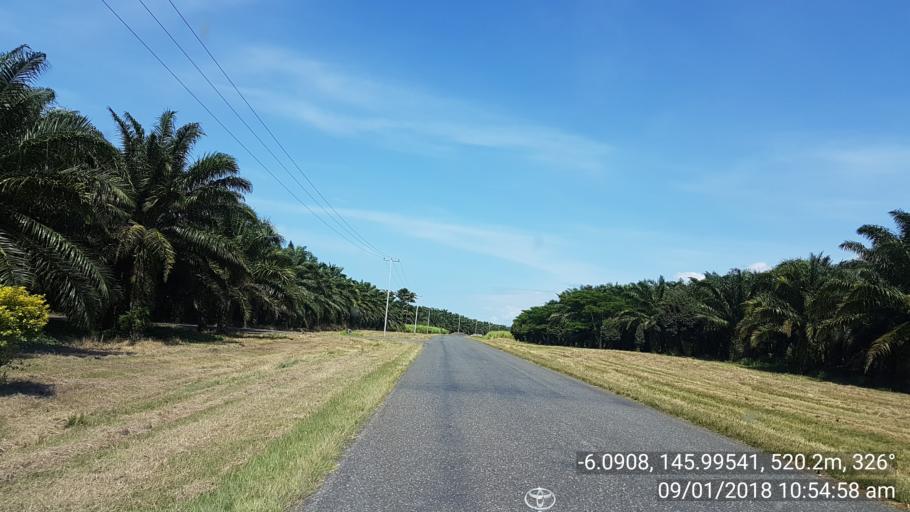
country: PG
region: Eastern Highlands
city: Kainantu
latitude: -6.0908
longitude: 145.9953
